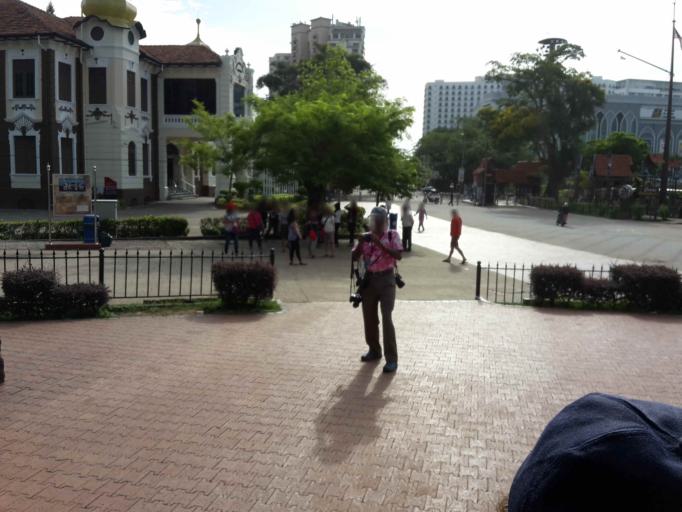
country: MY
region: Melaka
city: Malacca
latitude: 2.1917
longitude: 102.2504
